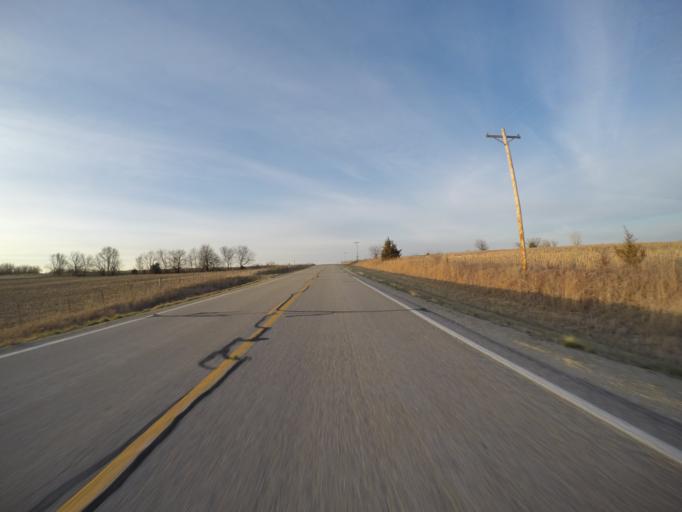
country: US
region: Kansas
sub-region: Clay County
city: Clay Center
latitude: 39.4215
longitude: -96.8488
